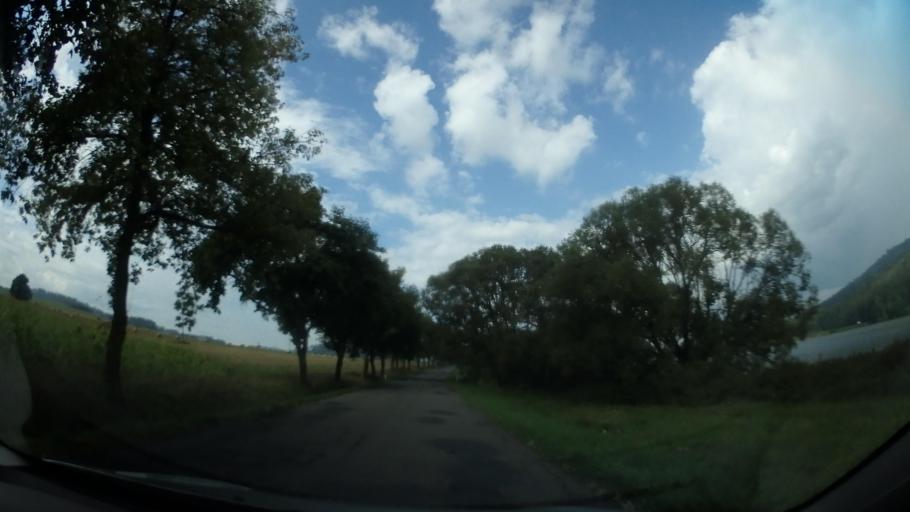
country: CZ
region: Plzensky
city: Horazd'ovice
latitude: 49.2630
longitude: 13.6584
